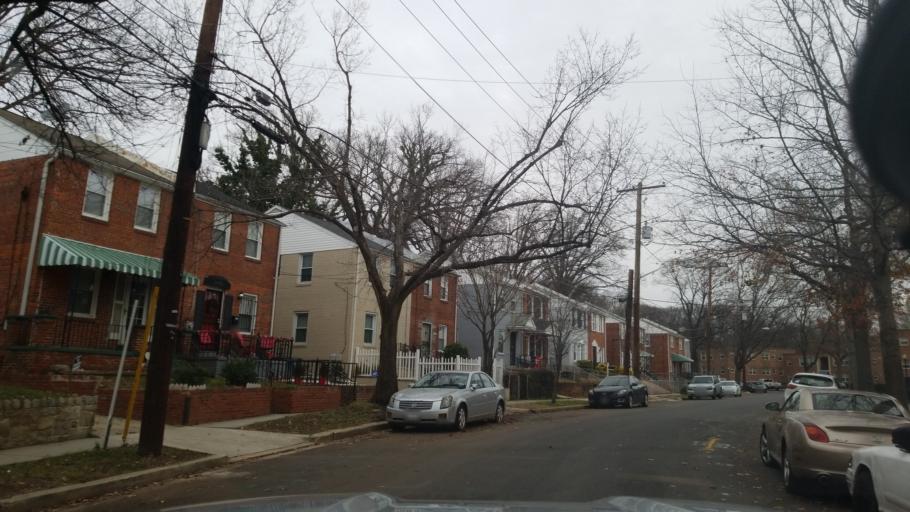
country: US
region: Maryland
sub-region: Prince George's County
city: Hillcrest Heights
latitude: 38.8465
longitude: -76.9699
